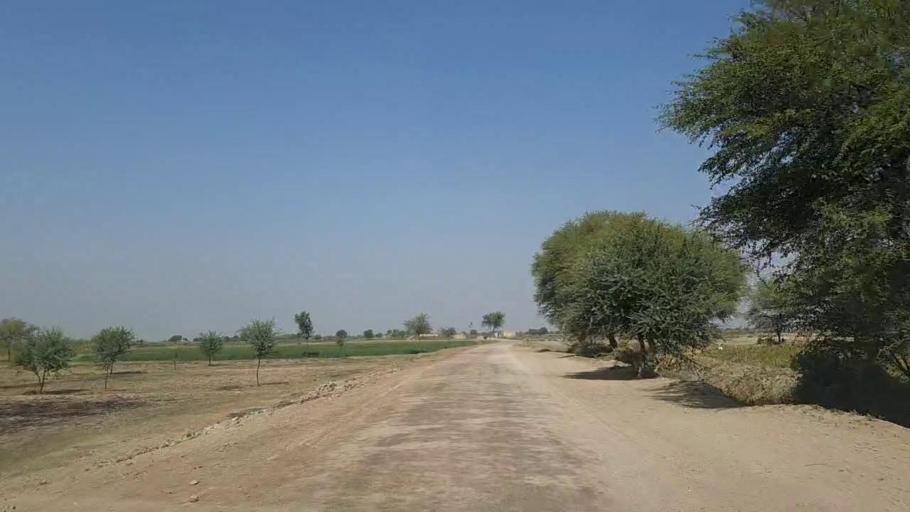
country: PK
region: Sindh
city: Samaro
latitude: 25.2155
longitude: 69.4043
